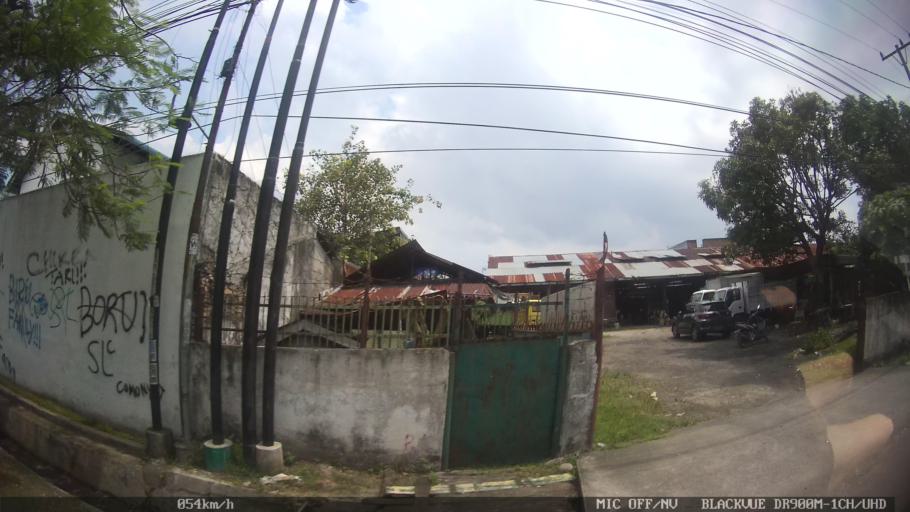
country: ID
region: North Sumatra
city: Medan
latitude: 3.6423
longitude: 98.6648
